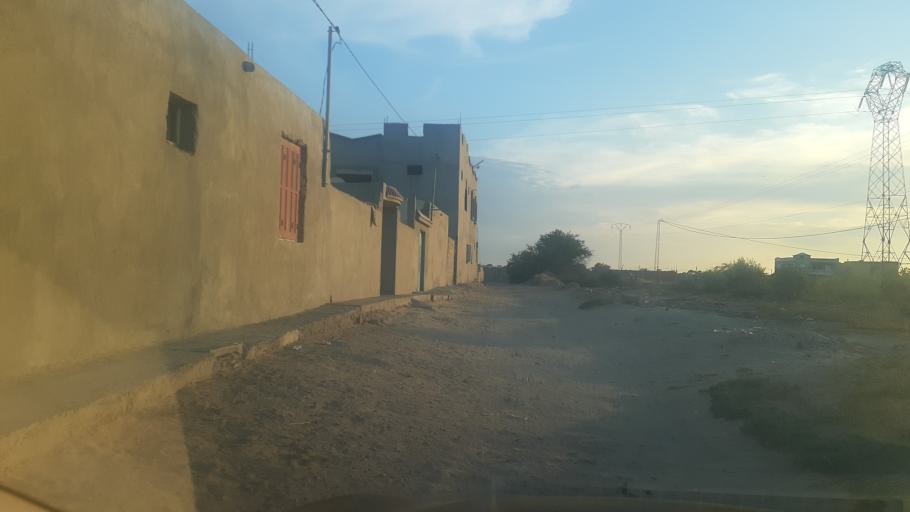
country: TN
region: Qabis
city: Gabes
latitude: 33.9337
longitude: 10.0393
